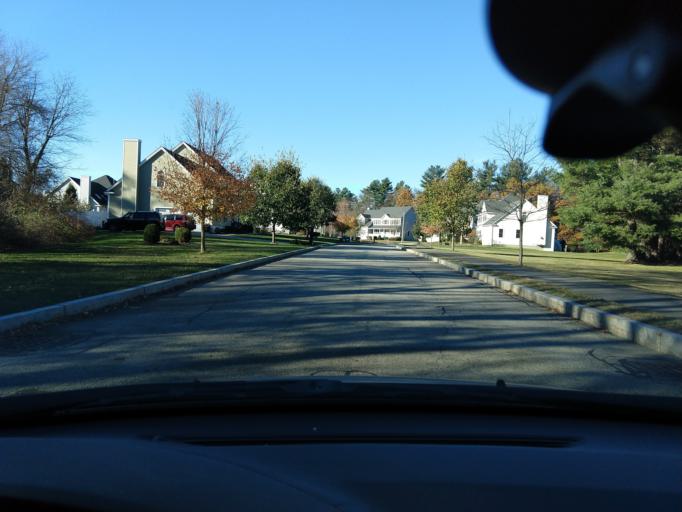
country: US
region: Massachusetts
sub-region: Middlesex County
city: Bedford
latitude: 42.4787
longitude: -71.2694
